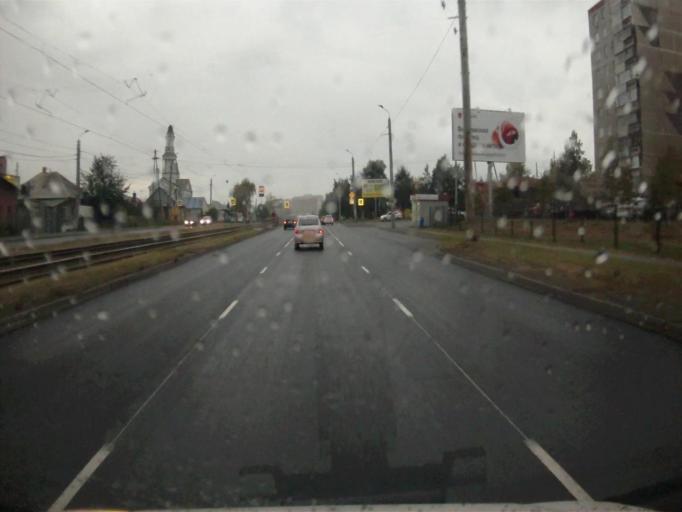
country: RU
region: Chelyabinsk
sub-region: Gorod Chelyabinsk
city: Chelyabinsk
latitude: 55.1846
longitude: 61.3693
